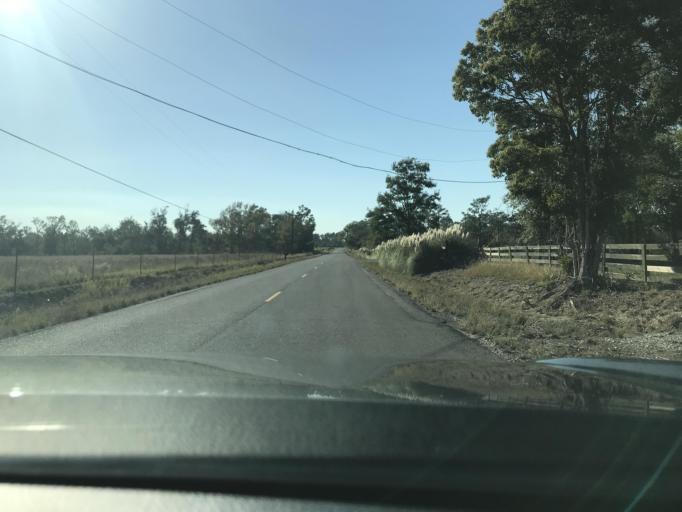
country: US
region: Louisiana
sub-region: Calcasieu Parish
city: Moss Bluff
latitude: 30.3153
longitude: -93.2631
